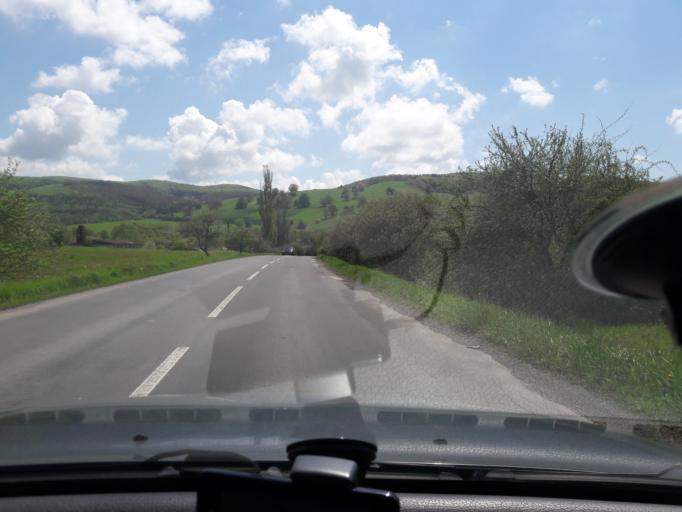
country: SK
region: Banskobystricky
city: Krupina
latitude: 48.4105
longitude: 19.1646
